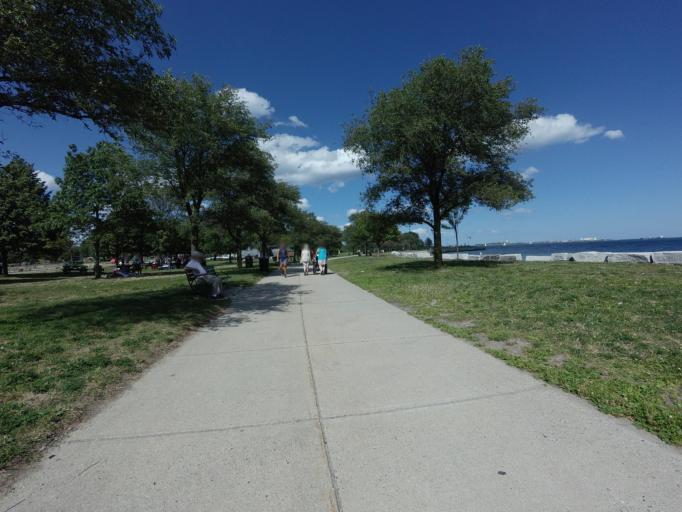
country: US
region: Massachusetts
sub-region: Suffolk County
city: South Boston
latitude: 42.3357
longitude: -71.0119
